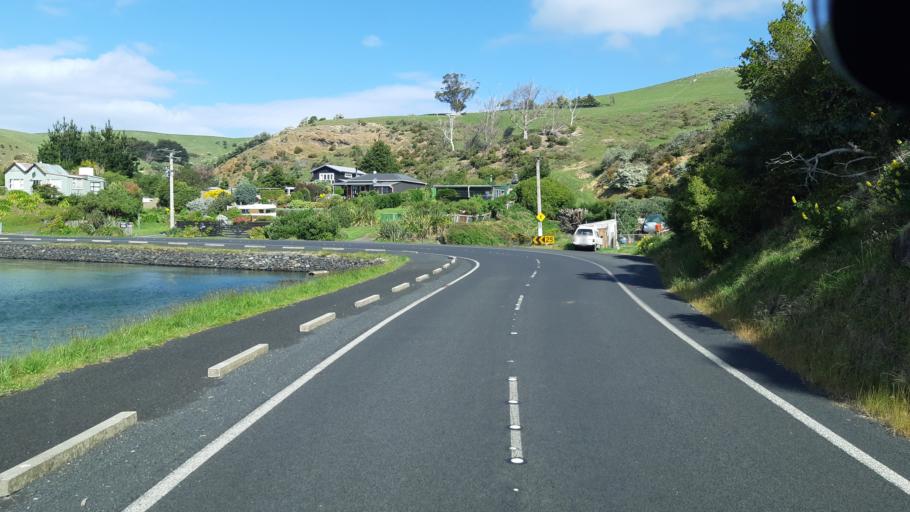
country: NZ
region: Otago
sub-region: Dunedin City
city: Portobello
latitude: -45.8010
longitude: 170.7061
